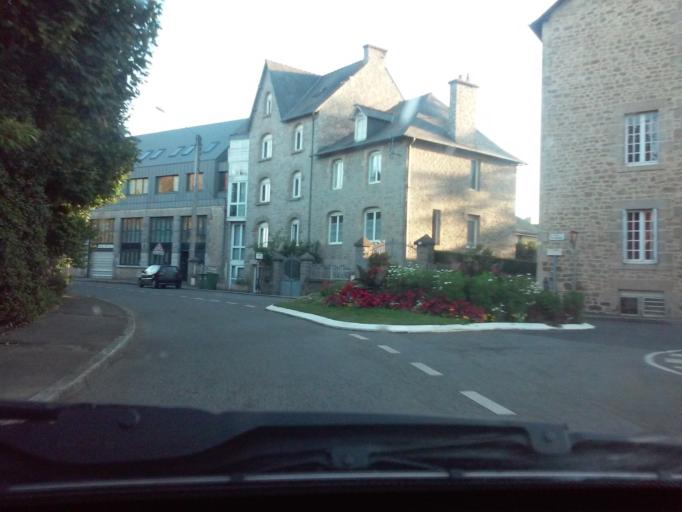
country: FR
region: Brittany
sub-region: Departement des Cotes-d'Armor
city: Lehon
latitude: 48.4595
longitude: -2.0497
